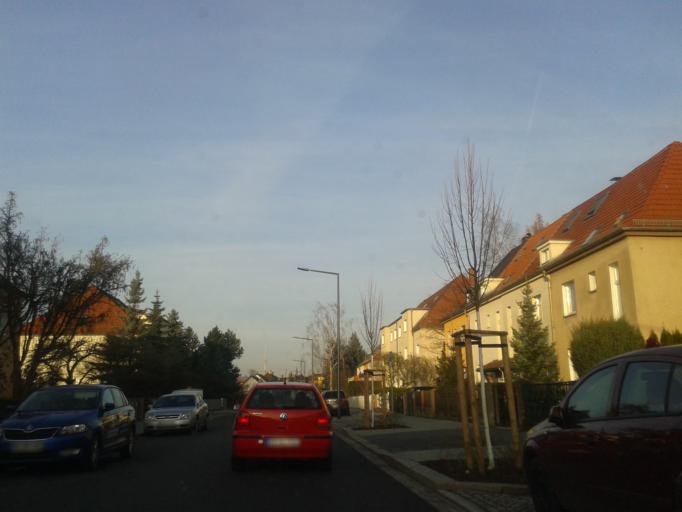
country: DE
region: Saxony
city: Heidenau
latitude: 51.0003
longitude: 13.8194
